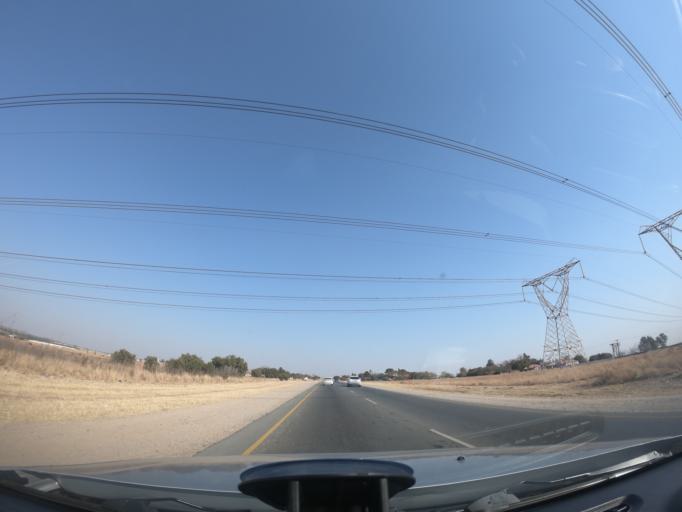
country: ZA
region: Gauteng
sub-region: City of Johannesburg Metropolitan Municipality
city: Diepsloot
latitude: -25.8969
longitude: 28.0273
